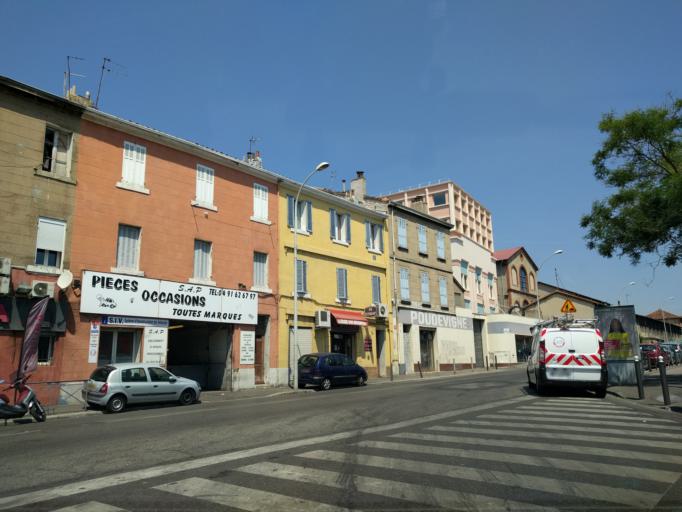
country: FR
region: Provence-Alpes-Cote d'Azur
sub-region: Departement des Bouches-du-Rhone
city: Marseille 03
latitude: 43.3205
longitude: 5.3677
